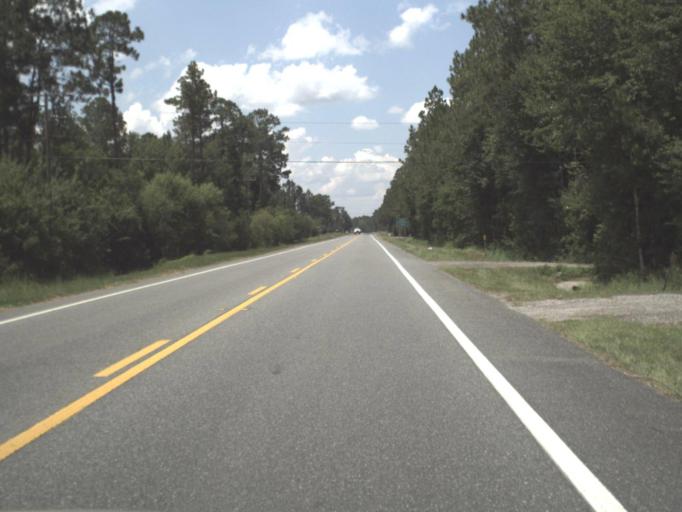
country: US
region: Florida
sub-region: Baker County
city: Macclenny
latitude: 30.3084
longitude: -82.1253
